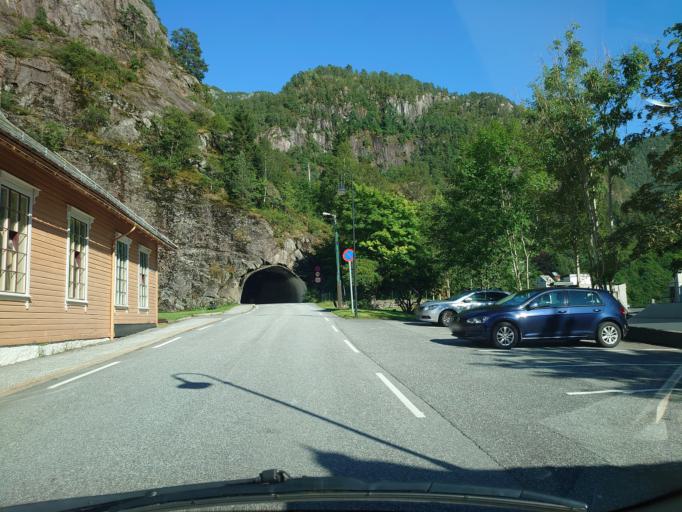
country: NO
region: Hordaland
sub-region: Vaksdal
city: Dale
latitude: 60.5900
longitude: 5.8237
